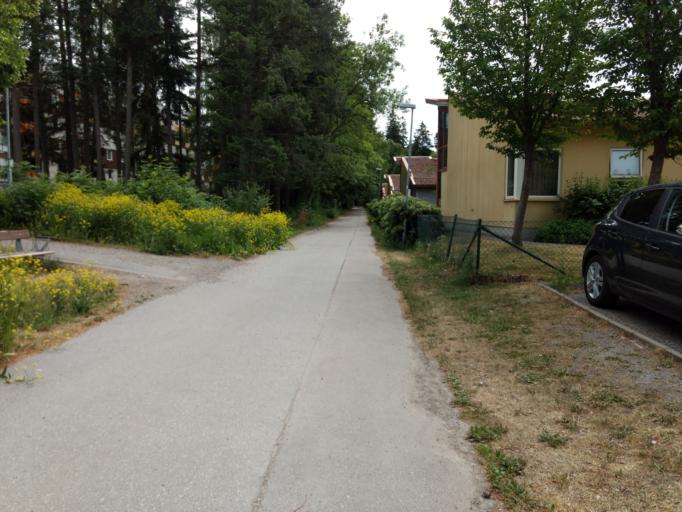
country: SE
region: Stockholm
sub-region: Upplands Vasby Kommun
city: Upplands Vaesby
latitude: 59.5293
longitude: 17.9092
